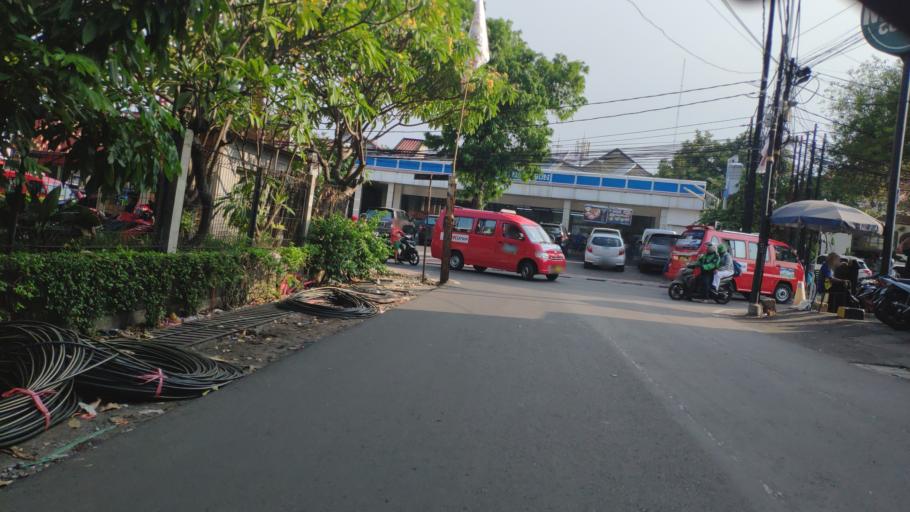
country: ID
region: Jakarta Raya
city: Jakarta
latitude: -6.2775
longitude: 106.8007
